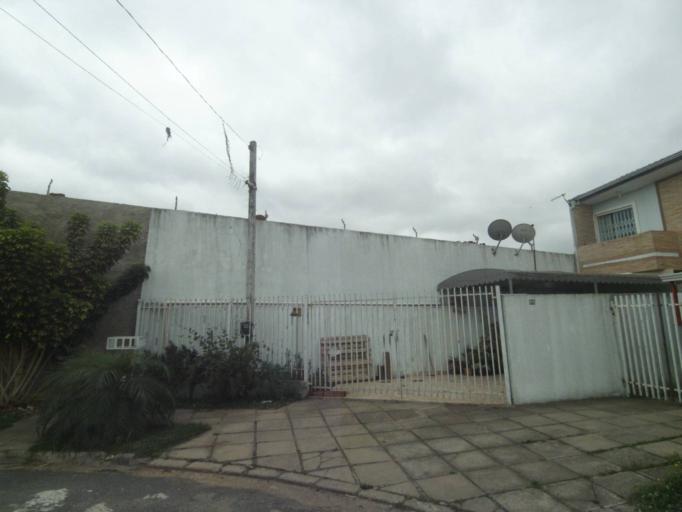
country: BR
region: Parana
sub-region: Sao Jose Dos Pinhais
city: Sao Jose dos Pinhais
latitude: -25.5552
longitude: -49.2680
